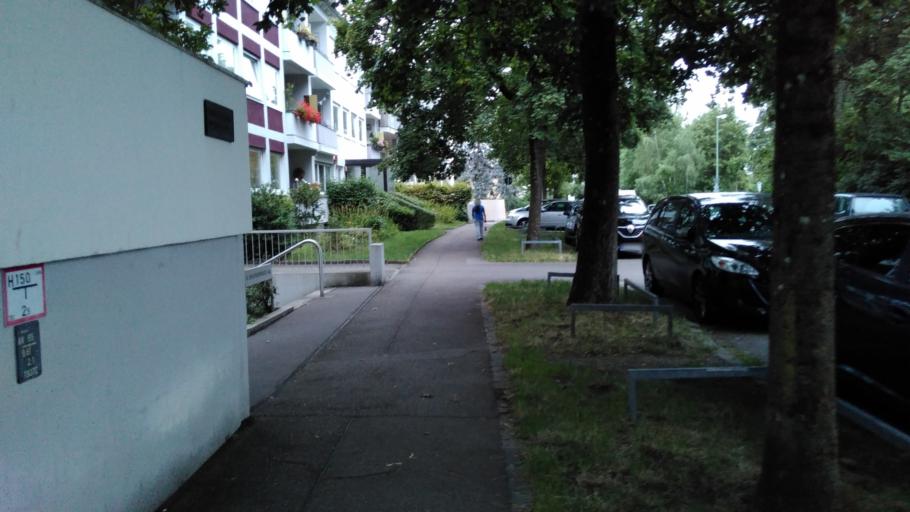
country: DE
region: Bavaria
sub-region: Swabia
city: Friedberg
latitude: 48.3562
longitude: 10.9511
